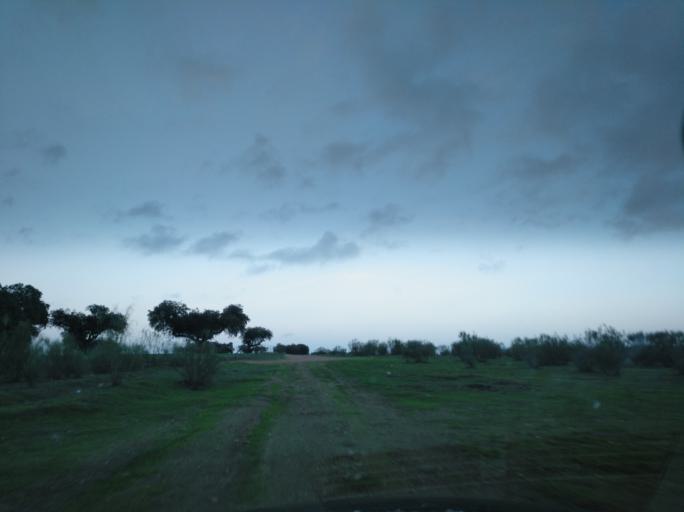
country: PT
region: Portalegre
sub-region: Campo Maior
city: Campo Maior
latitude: 39.1036
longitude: -7.1207
